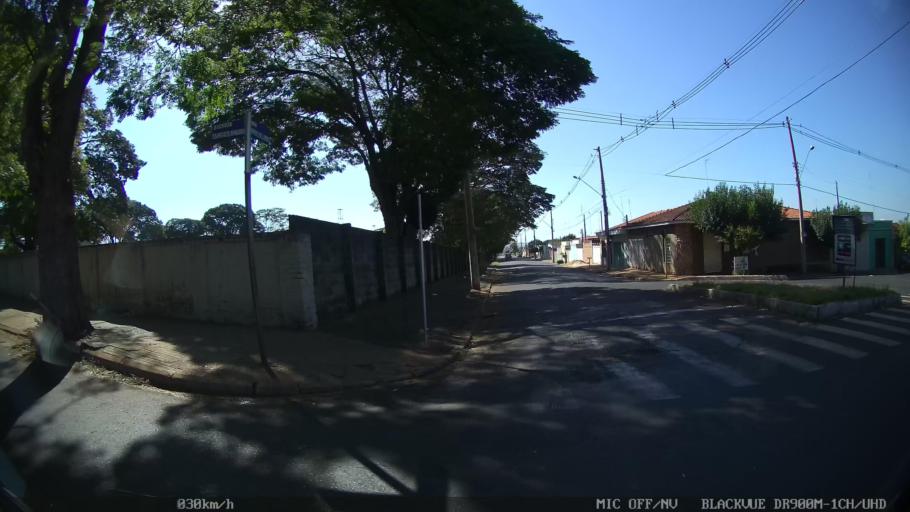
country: BR
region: Sao Paulo
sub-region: Batatais
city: Batatais
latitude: -20.9032
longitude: -47.5817
